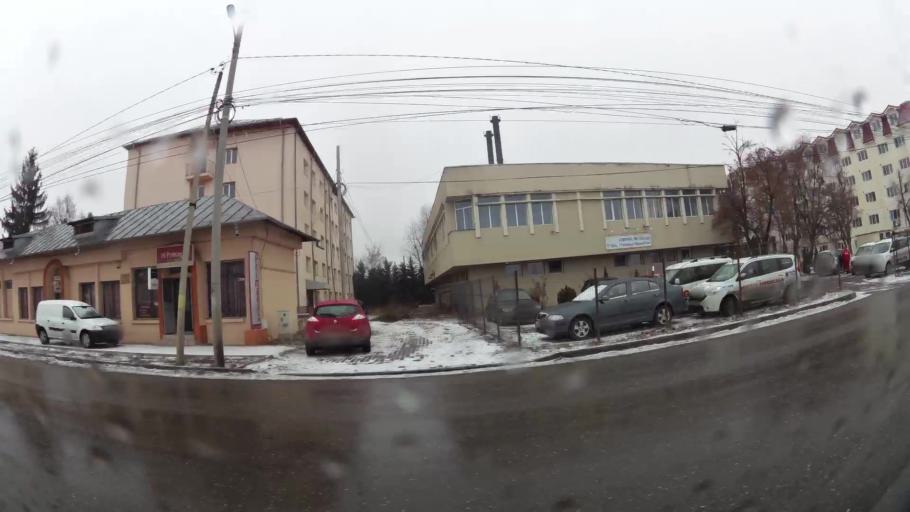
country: RO
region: Dambovita
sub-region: Municipiul Targoviste
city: Targoviste
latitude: 44.9156
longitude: 25.4410
